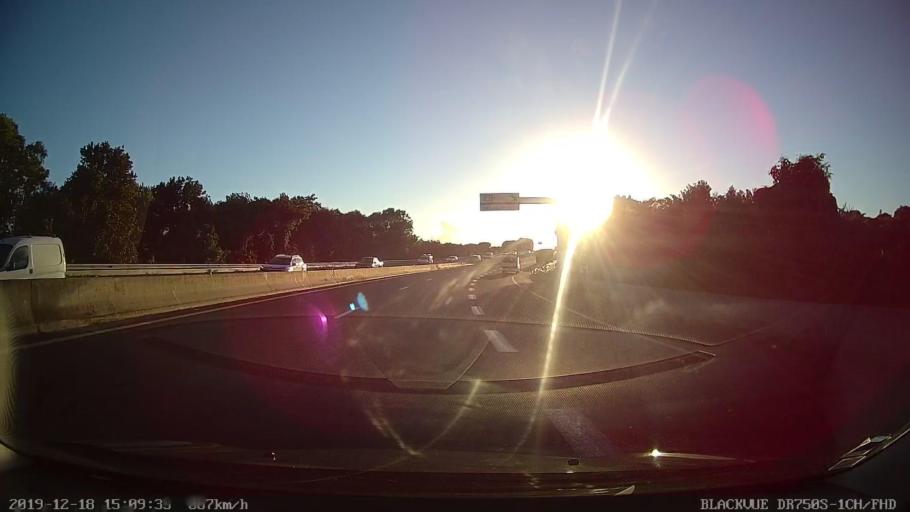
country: RE
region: Reunion
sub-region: Reunion
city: Sainte-Marie
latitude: -20.8981
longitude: 55.5767
